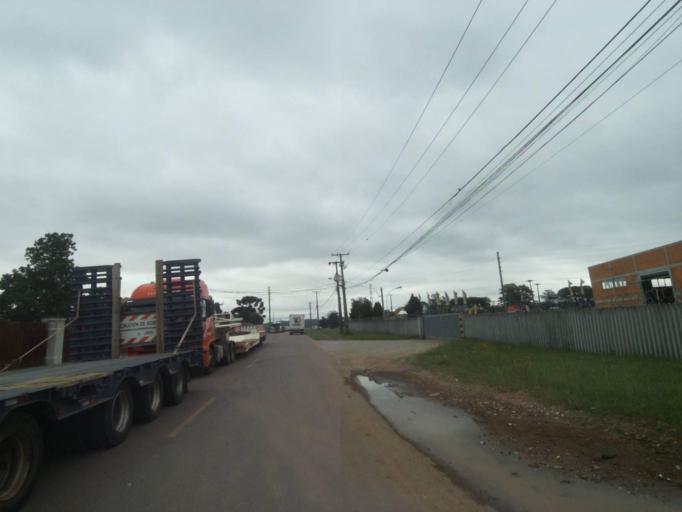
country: BR
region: Parana
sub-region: Araucaria
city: Araucaria
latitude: -25.5223
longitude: -49.3295
